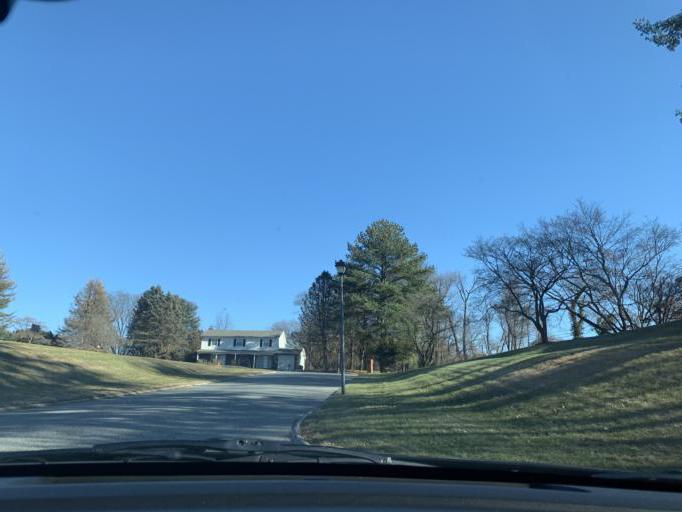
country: US
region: Maryland
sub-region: Baltimore County
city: Garrison
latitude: 39.3925
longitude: -76.7538
